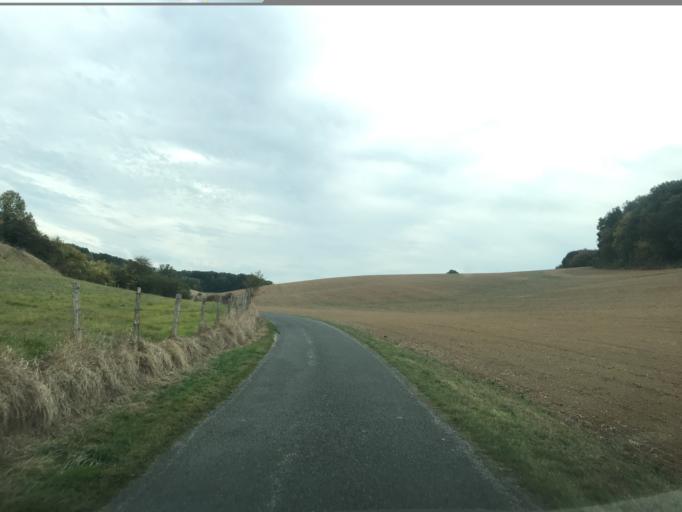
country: FR
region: Haute-Normandie
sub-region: Departement de l'Eure
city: Heudreville-sur-Eure
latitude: 49.0899
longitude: 1.2256
